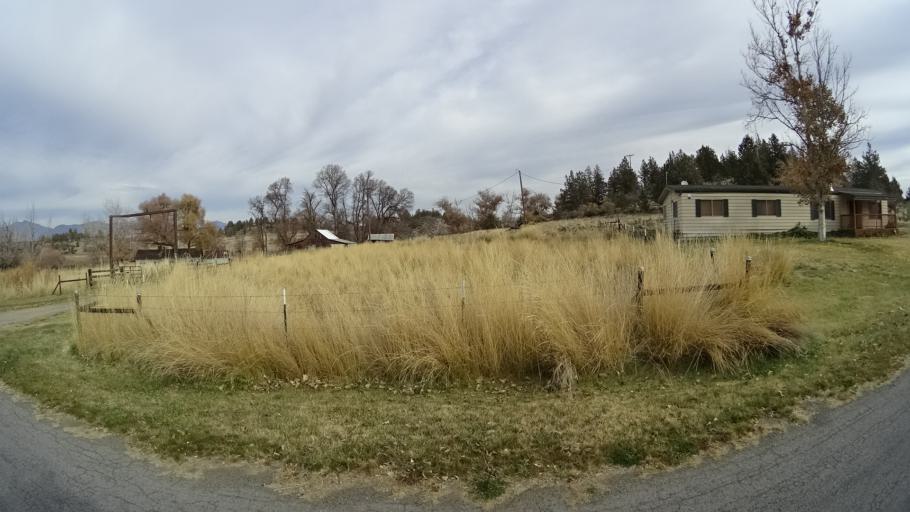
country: US
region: California
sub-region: Siskiyou County
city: Montague
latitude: 41.6827
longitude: -122.5273
